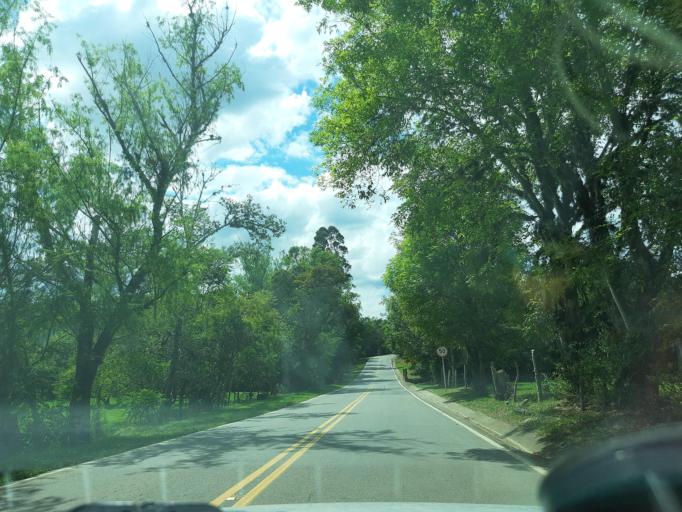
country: CO
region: Boyaca
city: Raquira
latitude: 5.5687
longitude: -73.6582
